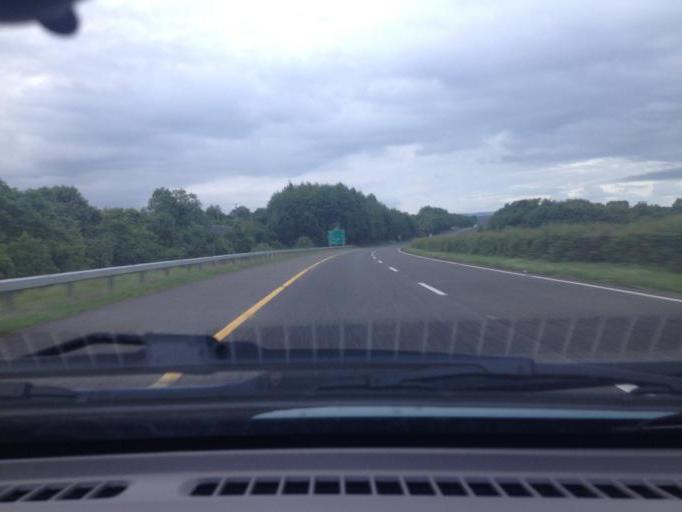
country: IE
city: Ballisodare
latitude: 54.2268
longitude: -8.4987
